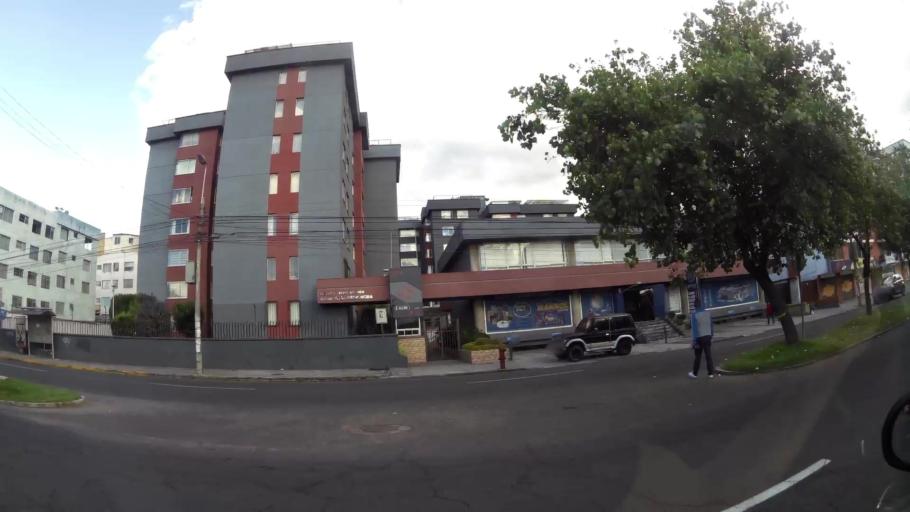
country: EC
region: Pichincha
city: Quito
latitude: -0.1572
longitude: -78.4810
